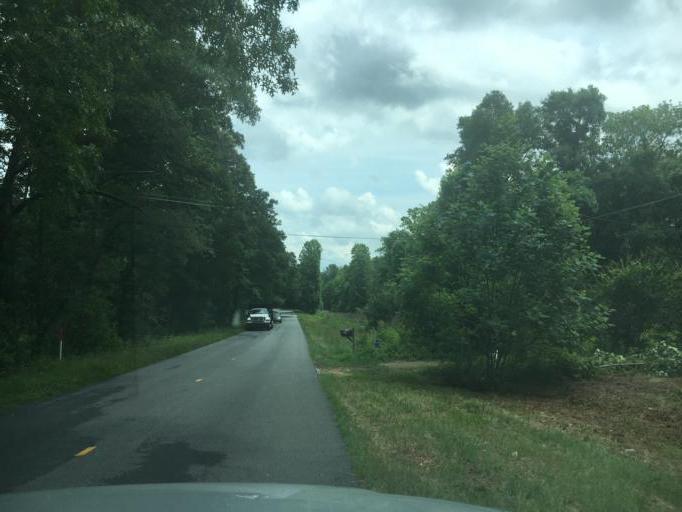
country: US
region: Georgia
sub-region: Franklin County
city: Gumlog
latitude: 34.4571
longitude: -83.0307
